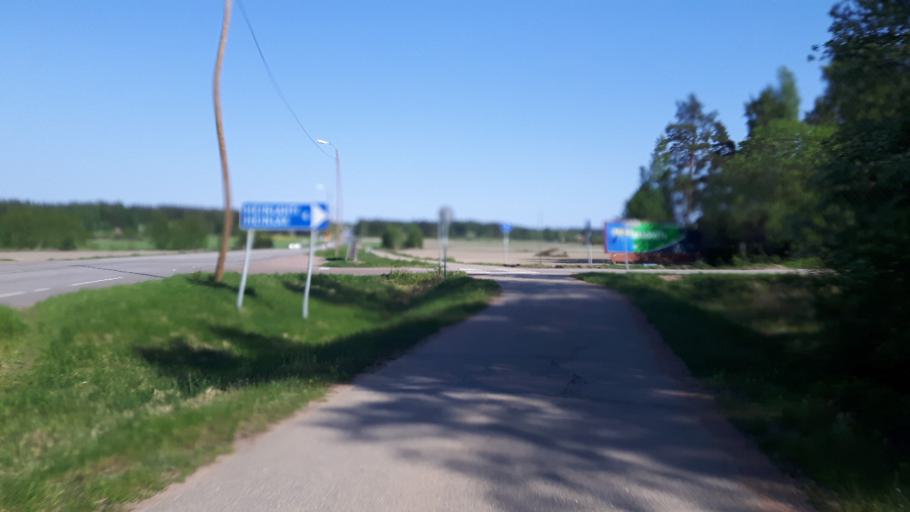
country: FI
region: Kymenlaakso
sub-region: Kotka-Hamina
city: Broby
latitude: 60.4968
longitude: 26.7913
